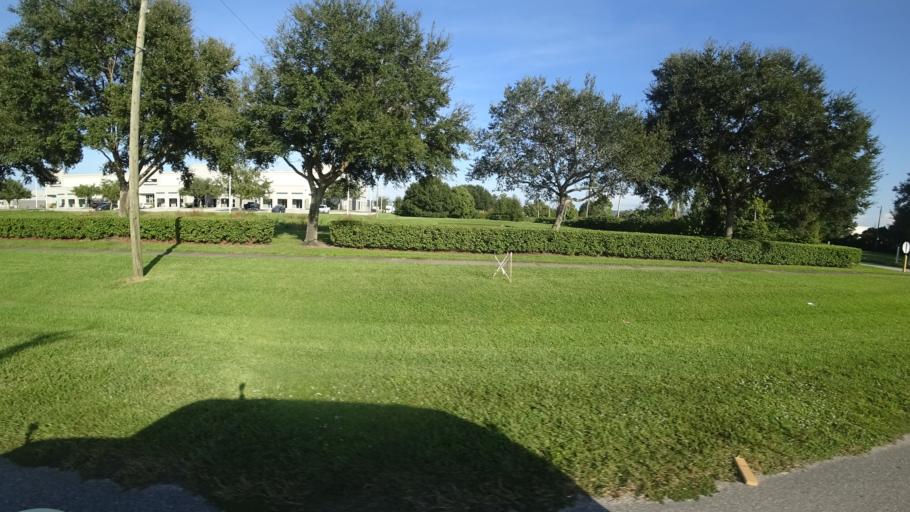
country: US
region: Florida
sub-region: Manatee County
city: Whitfield
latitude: 27.4113
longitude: -82.5467
